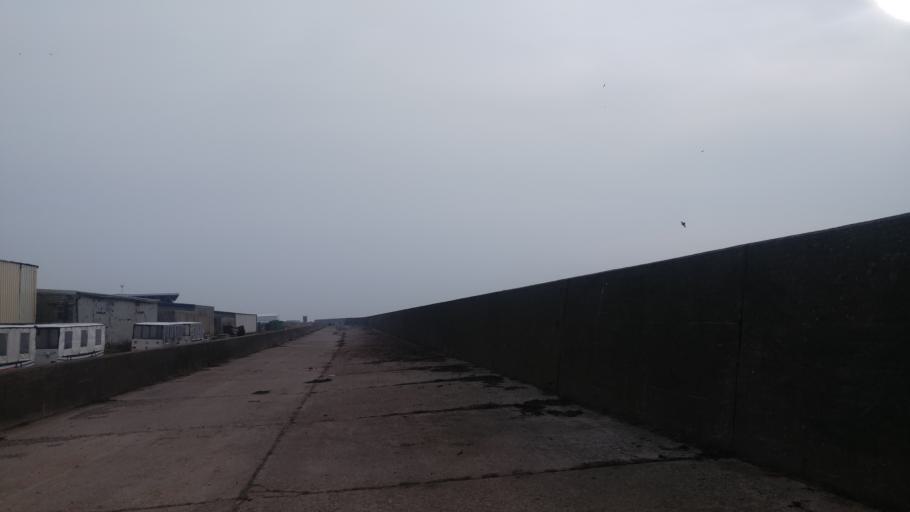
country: DE
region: Schleswig-Holstein
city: Helgoland
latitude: 54.1772
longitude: 7.8874
